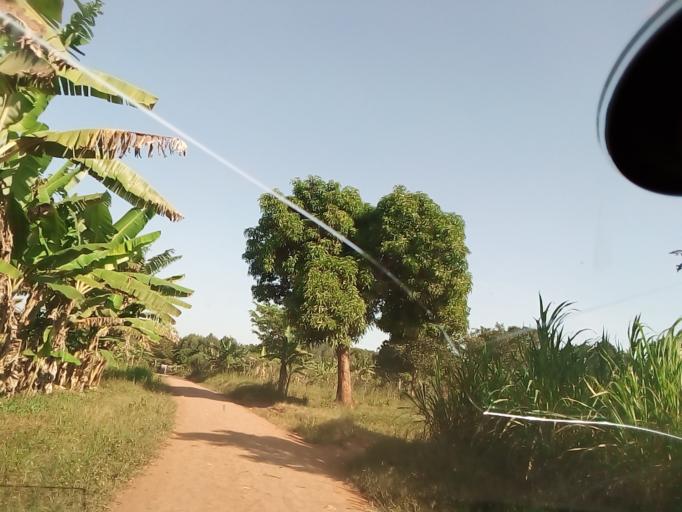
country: UG
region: Central Region
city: Masaka
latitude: -0.2696
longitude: 31.7220
